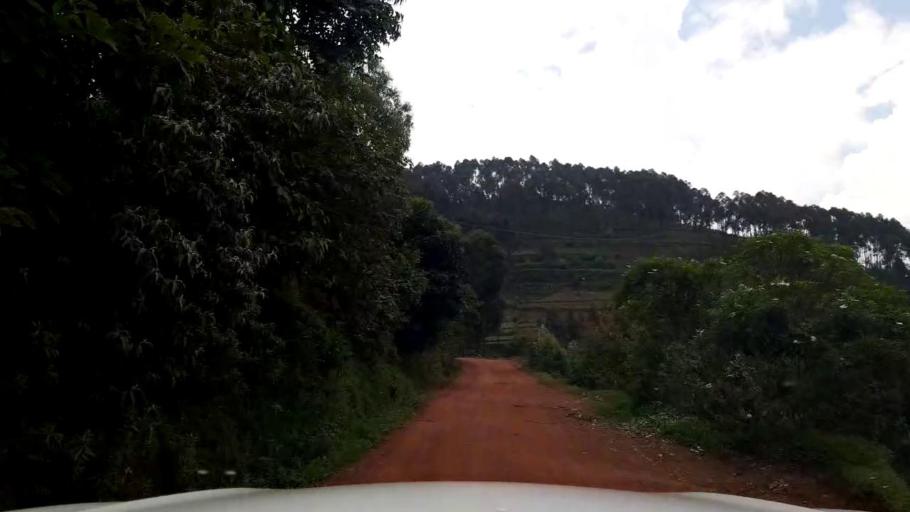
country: RW
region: Northern Province
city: Byumba
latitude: -1.5271
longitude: 29.9605
